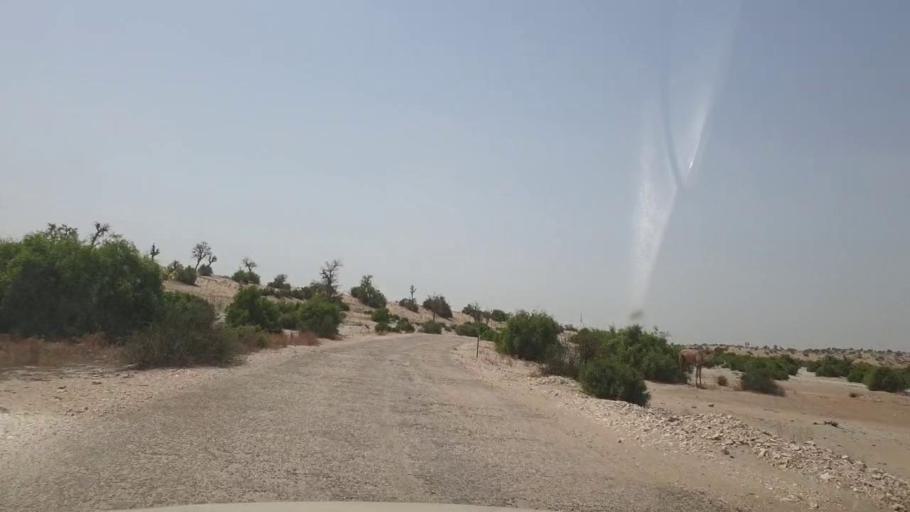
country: PK
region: Sindh
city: Khanpur
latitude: 27.3573
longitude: 69.3178
